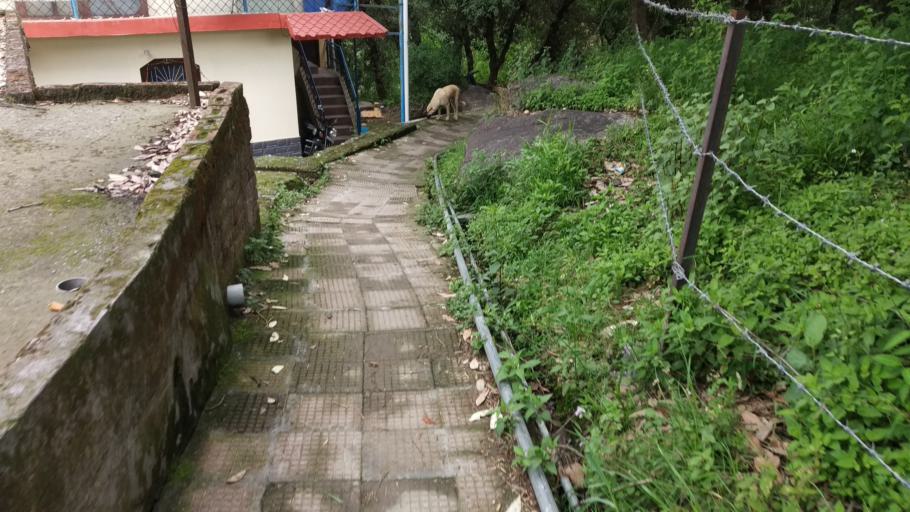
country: IN
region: Himachal Pradesh
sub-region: Kangra
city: Dharmsala
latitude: 32.1730
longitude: 76.3888
